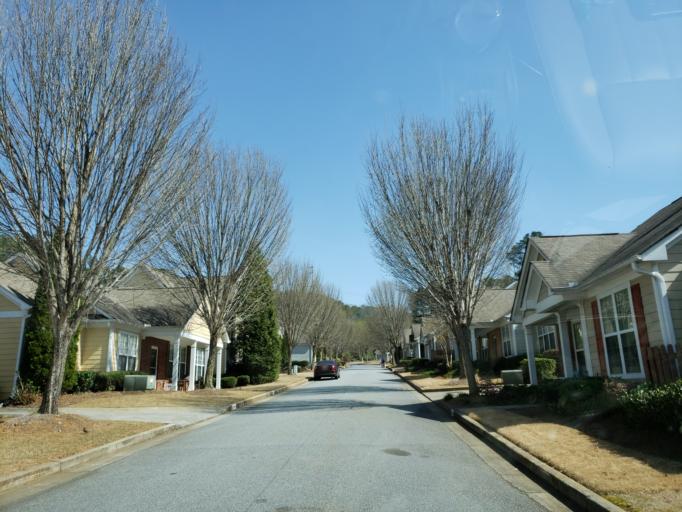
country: US
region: Georgia
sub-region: Cobb County
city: Marietta
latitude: 34.0082
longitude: -84.5482
